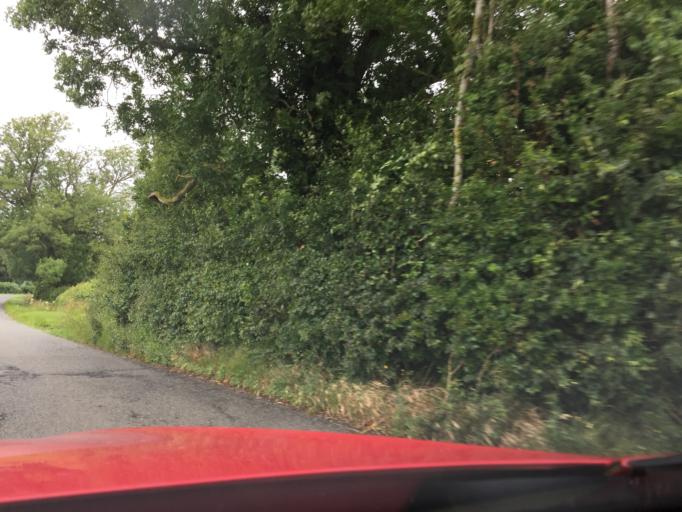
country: GB
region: England
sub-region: Northamptonshire
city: Daventry
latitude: 52.2402
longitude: -1.1790
